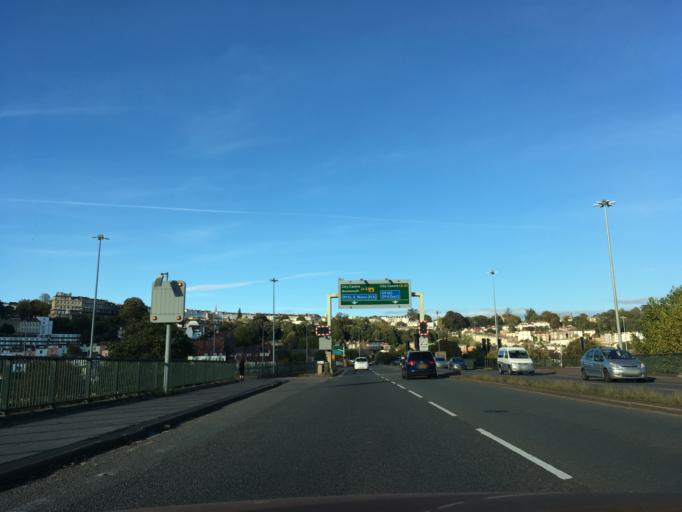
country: GB
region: England
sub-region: Bristol
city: Bristol
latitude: 51.4471
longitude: -2.6237
